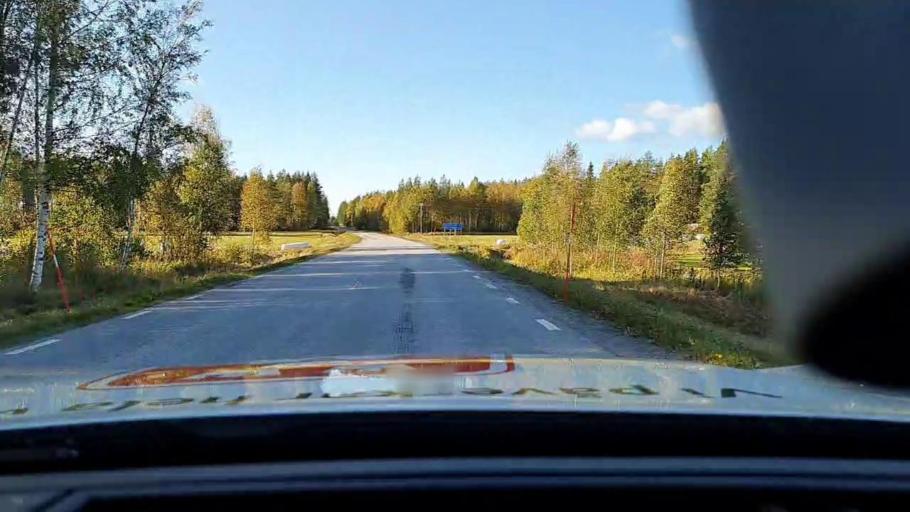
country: SE
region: Norrbotten
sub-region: Pitea Kommun
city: Norrfjarden
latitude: 65.4338
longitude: 21.4846
